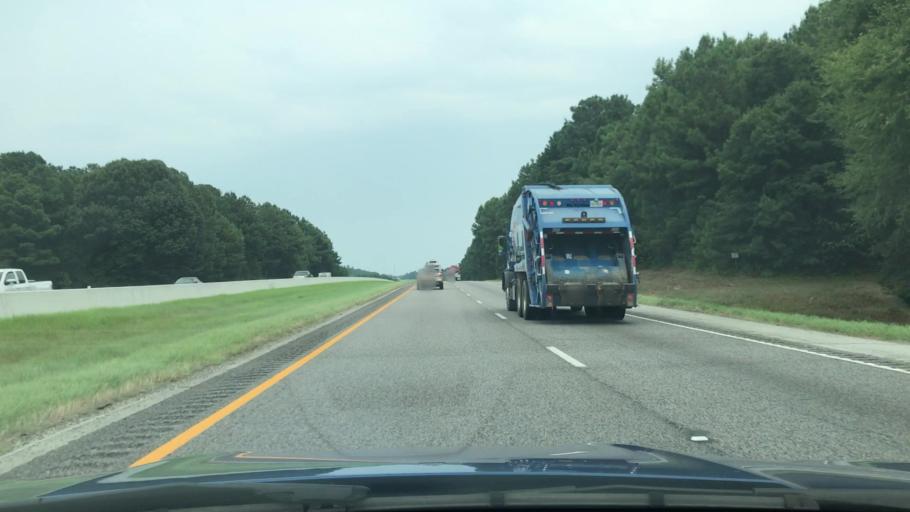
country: US
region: Texas
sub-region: Smith County
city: Lindale
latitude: 32.4604
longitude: -95.3191
